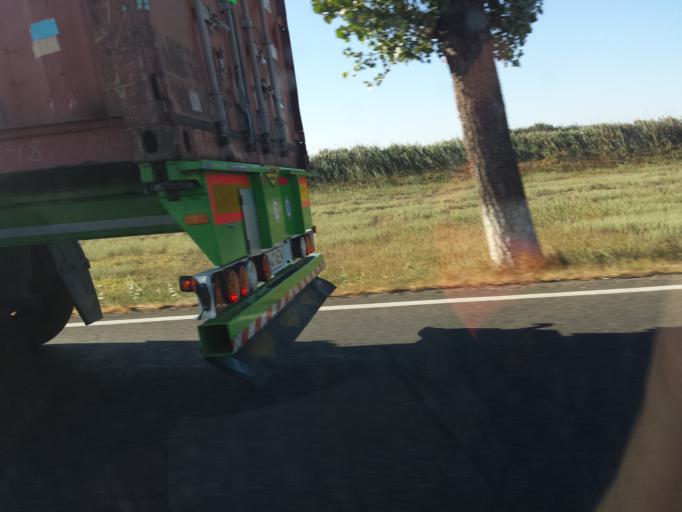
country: RO
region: Ialomita
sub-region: Comuna Cosambesti
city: Cosambesti
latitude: 44.5849
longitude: 27.4303
